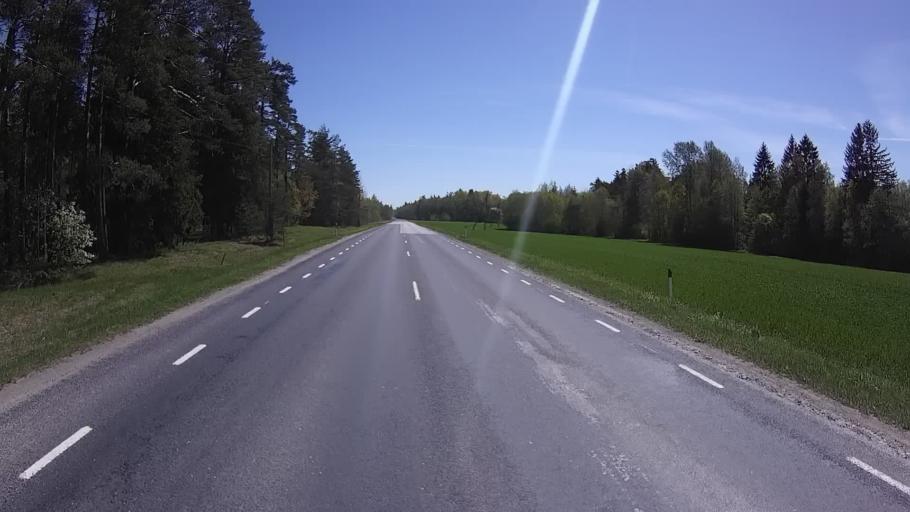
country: EE
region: Harju
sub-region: Raasiku vald
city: Raasiku
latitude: 59.1529
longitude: 25.1942
